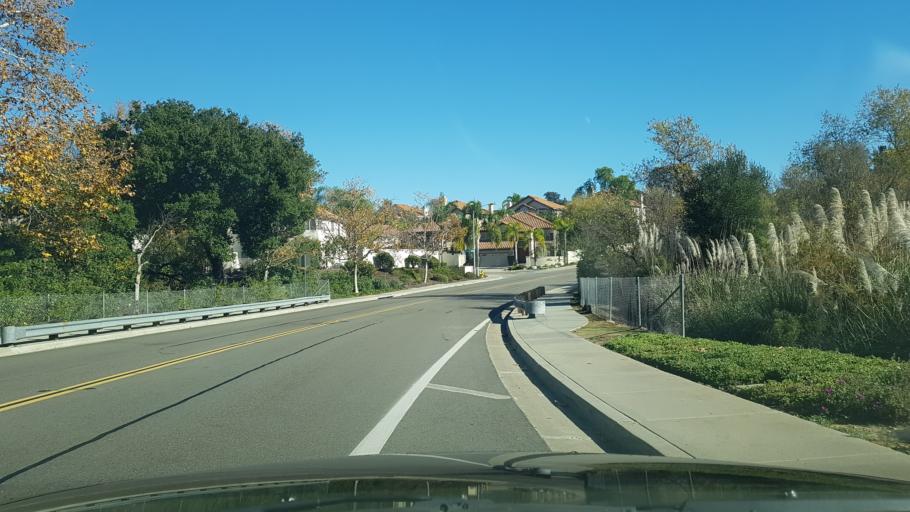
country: US
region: California
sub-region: San Diego County
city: Escondido
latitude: 33.0398
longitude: -117.0883
